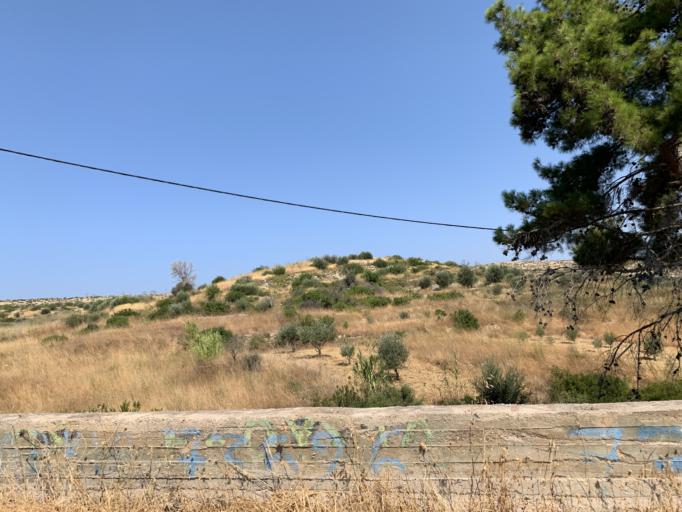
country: GR
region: North Aegean
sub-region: Chios
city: Thymiana
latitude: 38.3056
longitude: 25.9995
